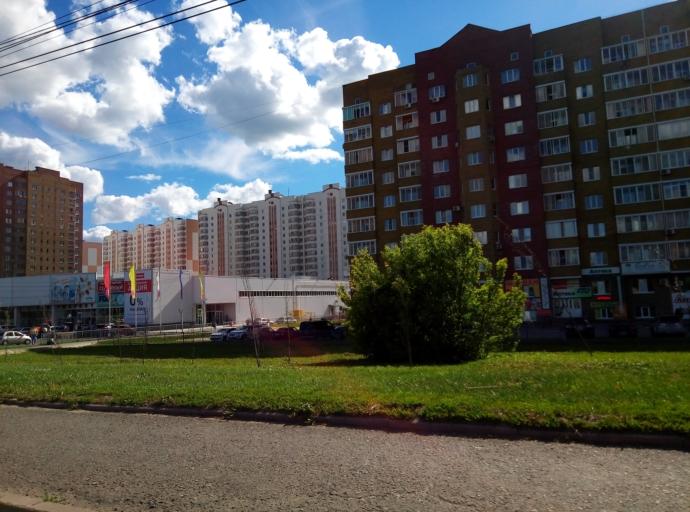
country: RU
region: Kursk
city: Kursk
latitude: 51.7829
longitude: 36.1727
